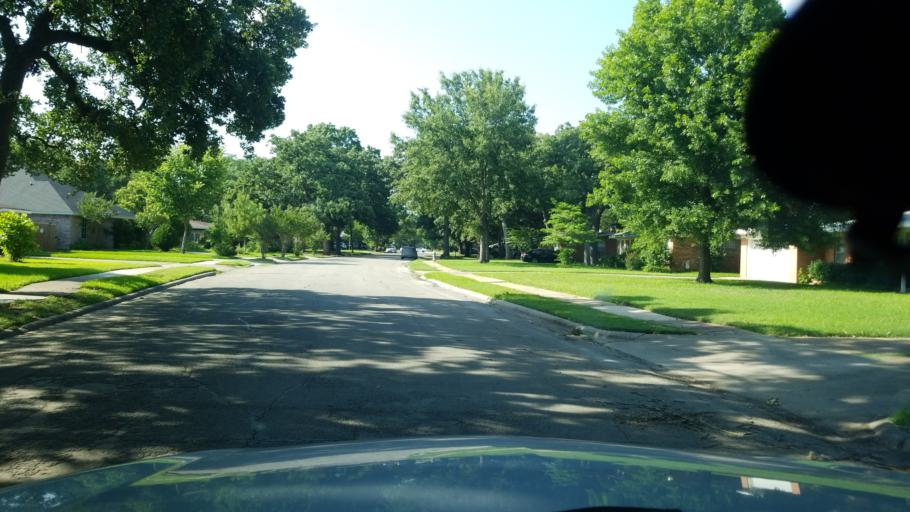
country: US
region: Texas
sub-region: Dallas County
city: Irving
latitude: 32.8205
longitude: -96.9704
